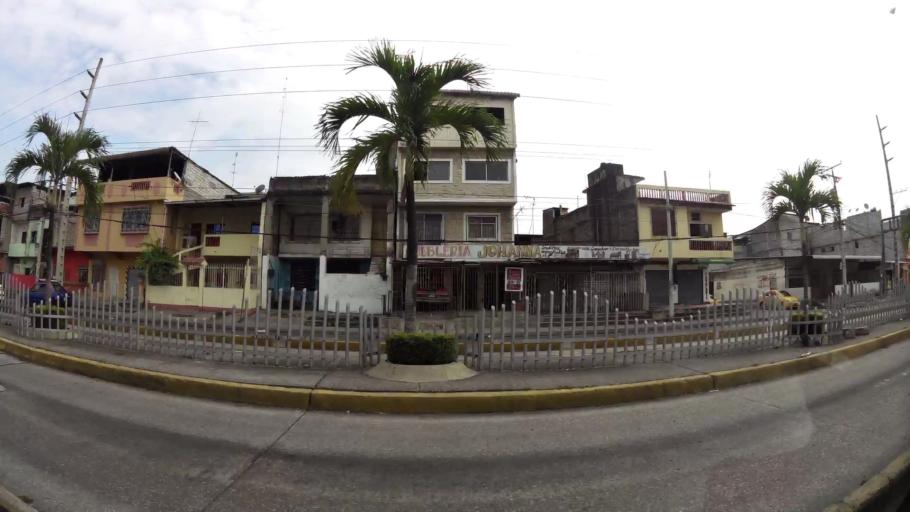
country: EC
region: Guayas
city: Guayaquil
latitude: -2.2511
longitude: -79.8894
